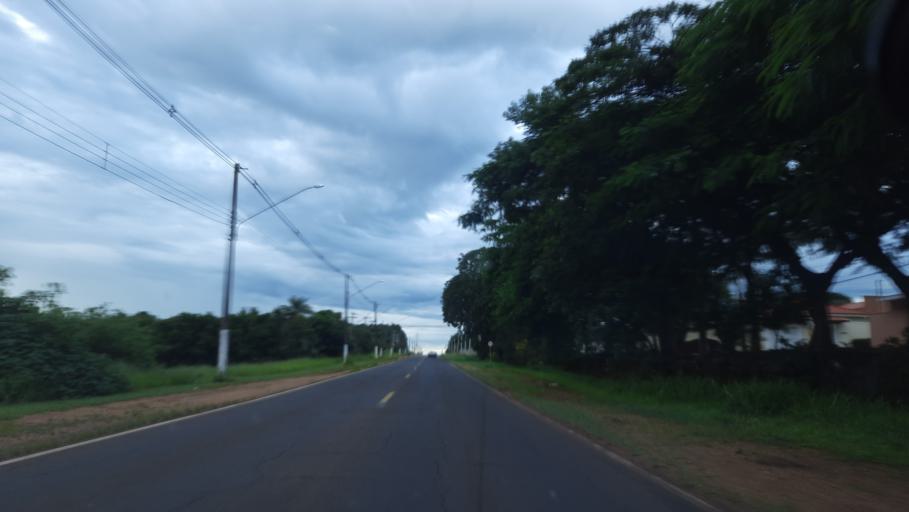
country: BR
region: Sao Paulo
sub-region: Casa Branca
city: Casa Branca
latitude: -21.7762
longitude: -47.0713
